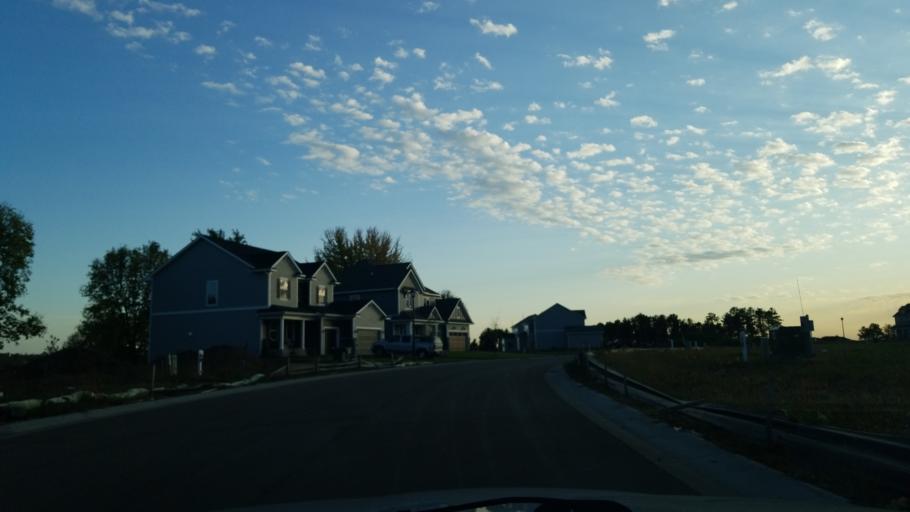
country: US
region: Wisconsin
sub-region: Saint Croix County
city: Hudson
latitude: 44.9685
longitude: -92.7262
